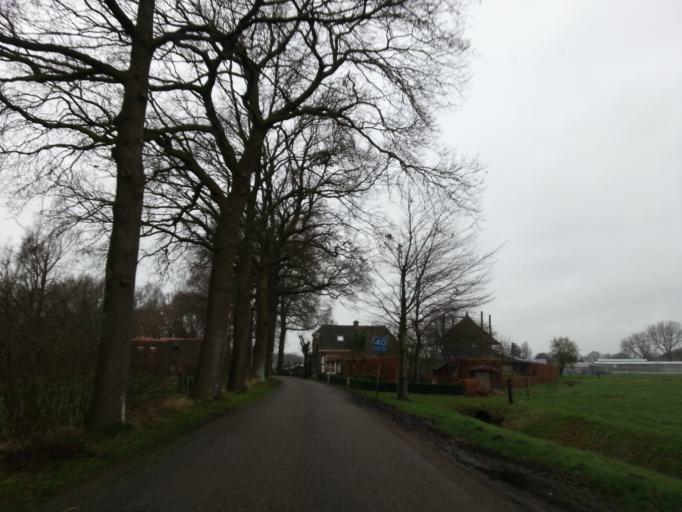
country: NL
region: Overijssel
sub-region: Gemeente Dalfsen
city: Dalfsen
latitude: 52.5151
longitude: 6.2345
